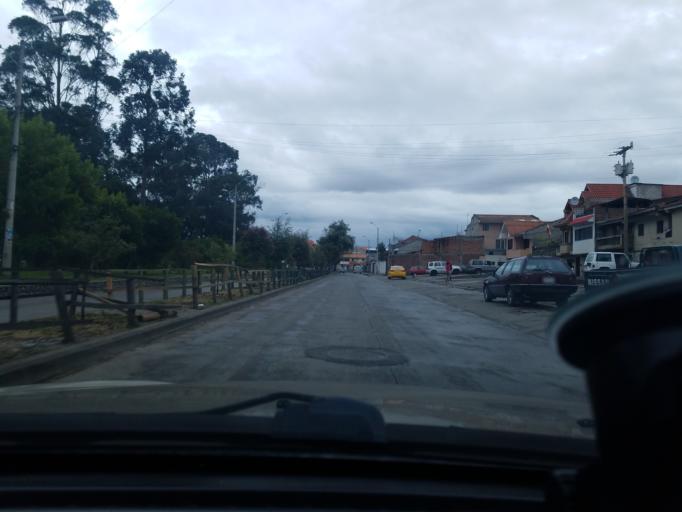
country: EC
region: Azuay
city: Cuenca
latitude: -2.9006
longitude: -78.9782
